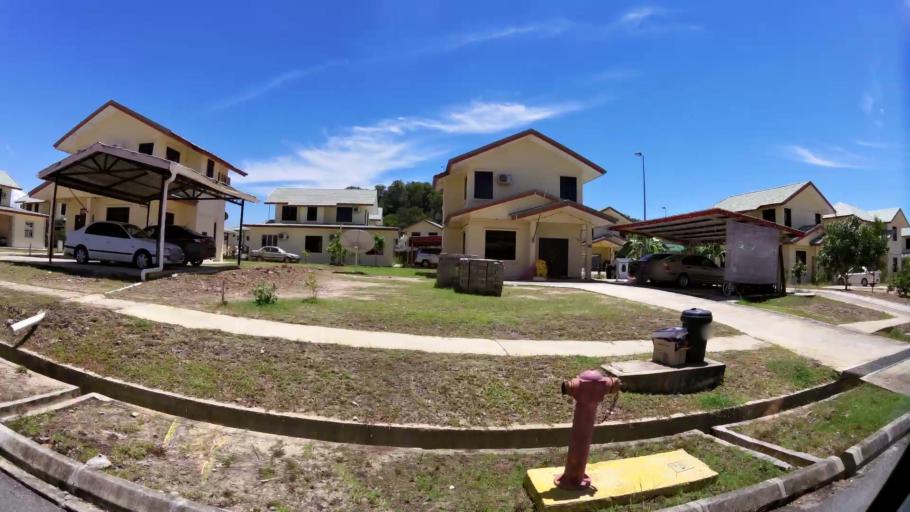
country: BN
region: Brunei and Muara
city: Bandar Seri Begawan
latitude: 5.0314
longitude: 115.0399
